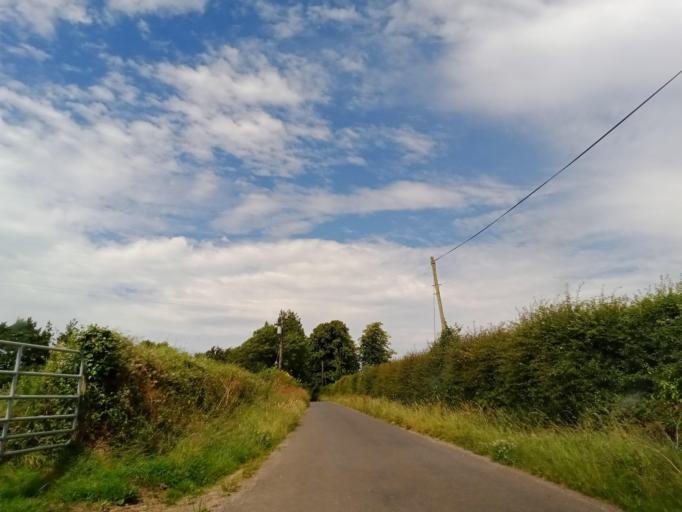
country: IE
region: Leinster
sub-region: Kilkenny
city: Thomastown
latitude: 52.5777
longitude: -7.1260
